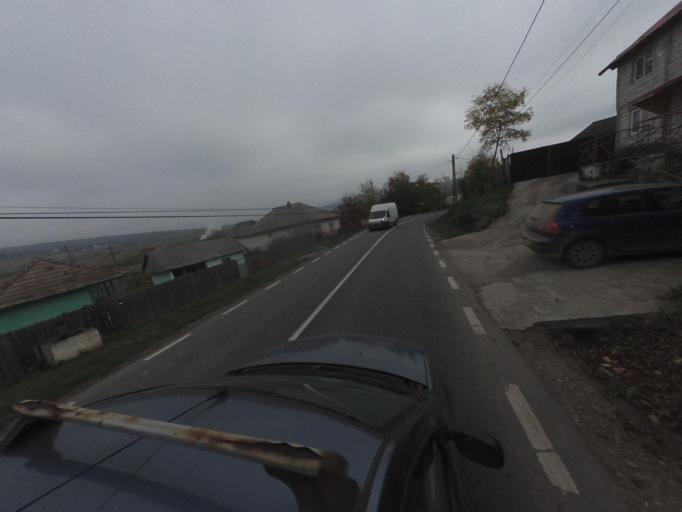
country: RO
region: Vaslui
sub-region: Comuna Bacesti
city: Bacesti
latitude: 46.8301
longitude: 27.2387
